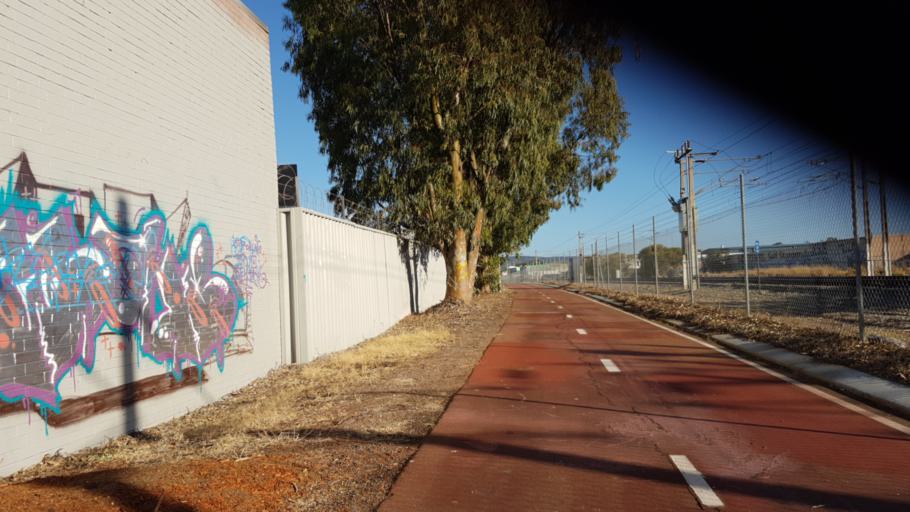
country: AU
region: Western Australia
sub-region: Gosnells
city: Maddington
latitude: -32.0462
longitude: 115.9780
